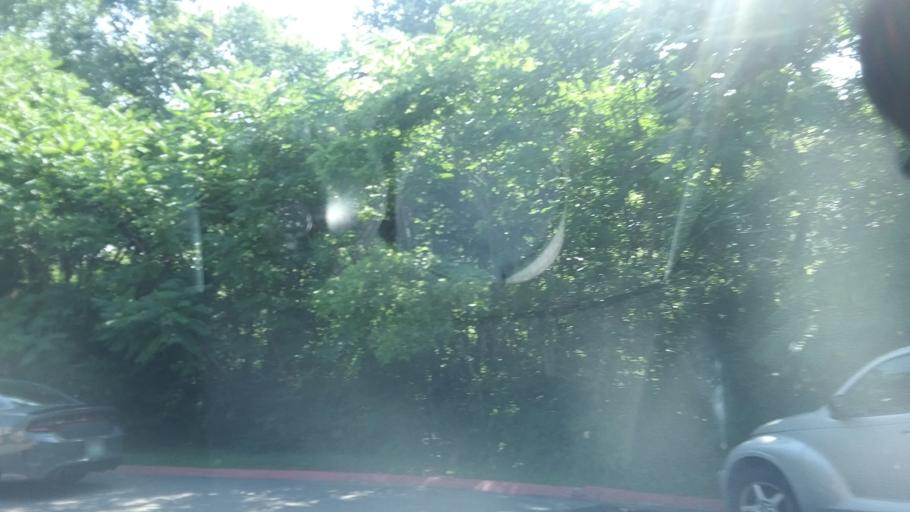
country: US
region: Tennessee
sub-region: Davidson County
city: Belle Meade
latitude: 36.1010
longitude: -86.9196
